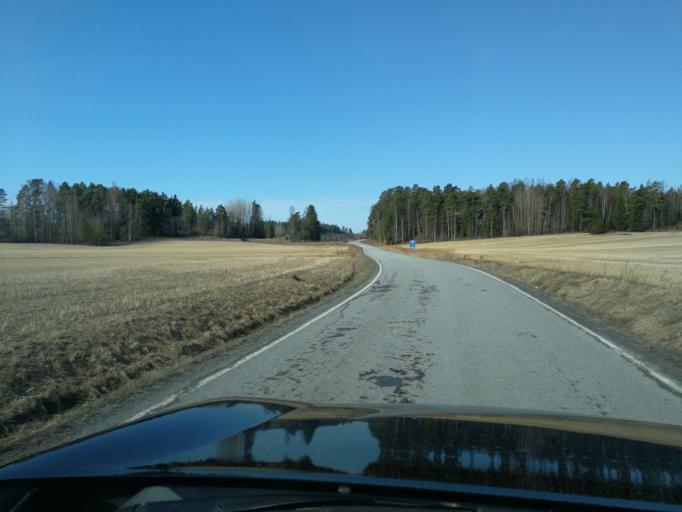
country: FI
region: Uusimaa
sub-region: Raaseporin
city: Inga
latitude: 60.0495
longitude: 24.0656
